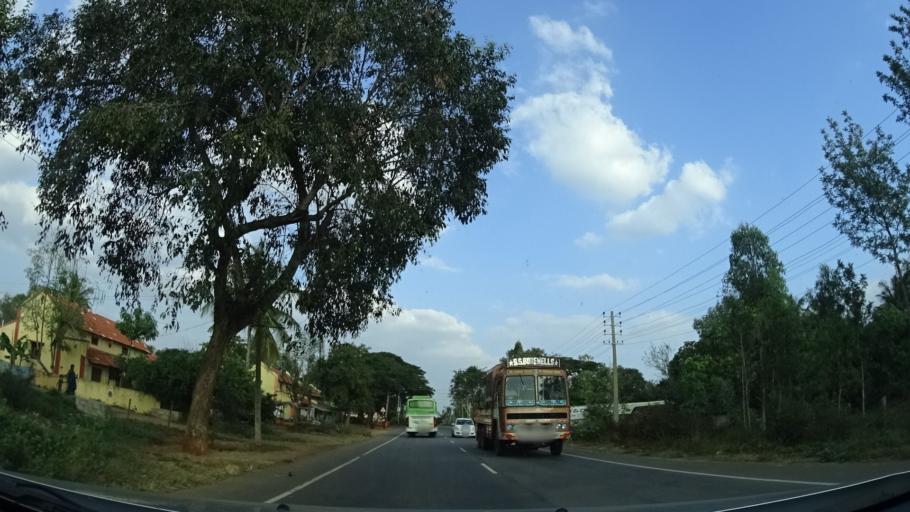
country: IN
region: Karnataka
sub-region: Mandya
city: Malavalli
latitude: 12.3708
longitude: 77.0180
